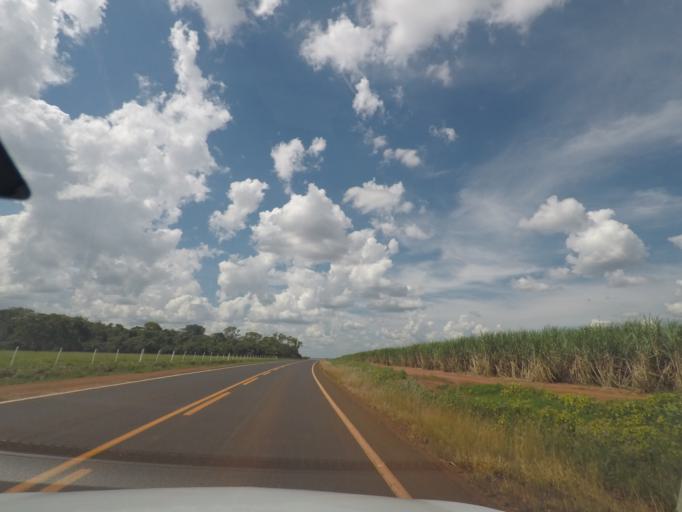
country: BR
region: Minas Gerais
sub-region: Conceicao Das Alagoas
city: Conceicao das Alagoas
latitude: -19.8502
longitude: -48.5977
